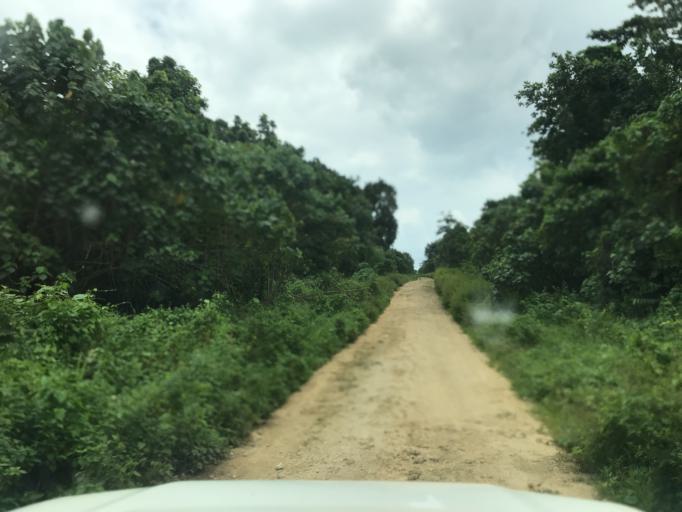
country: VU
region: Sanma
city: Port-Olry
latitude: -15.1875
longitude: 167.0051
